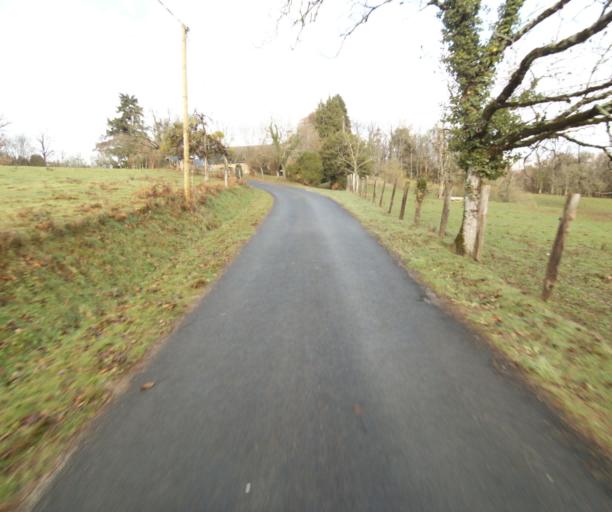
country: FR
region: Limousin
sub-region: Departement de la Correze
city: Saint-Mexant
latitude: 45.2496
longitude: 1.6351
